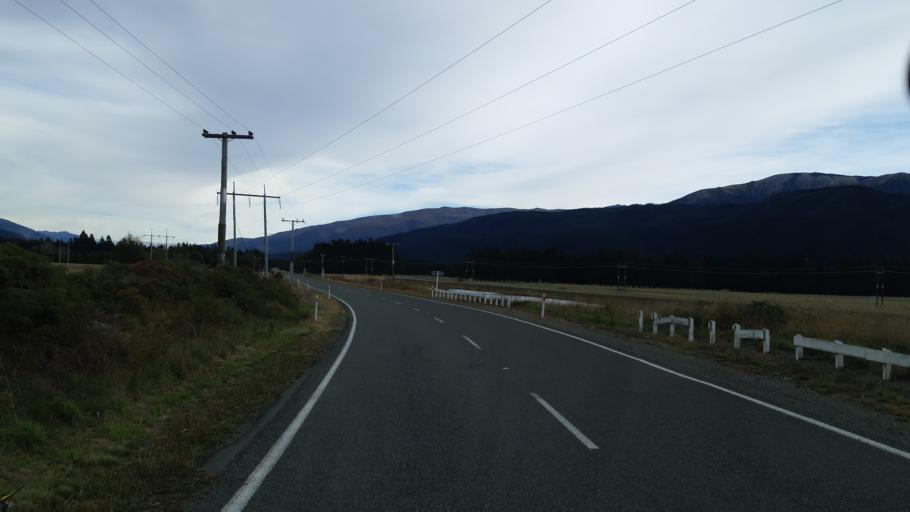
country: NZ
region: Tasman
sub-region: Tasman District
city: Brightwater
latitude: -41.6632
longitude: 173.2116
